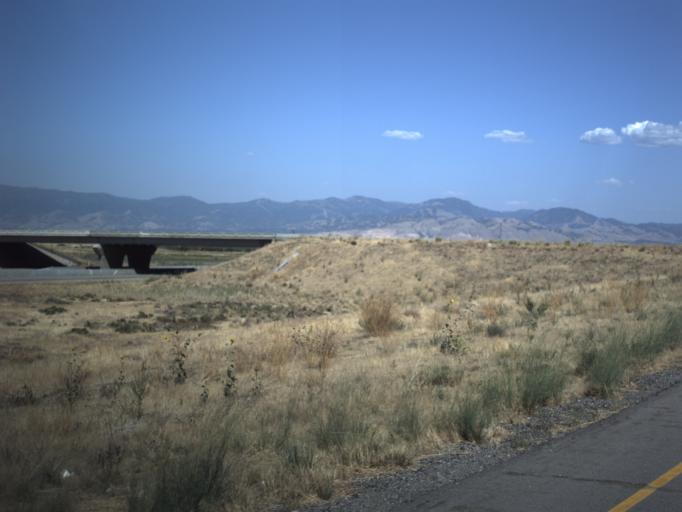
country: US
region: Utah
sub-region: Salt Lake County
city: Magna
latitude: 40.7700
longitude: -112.0647
